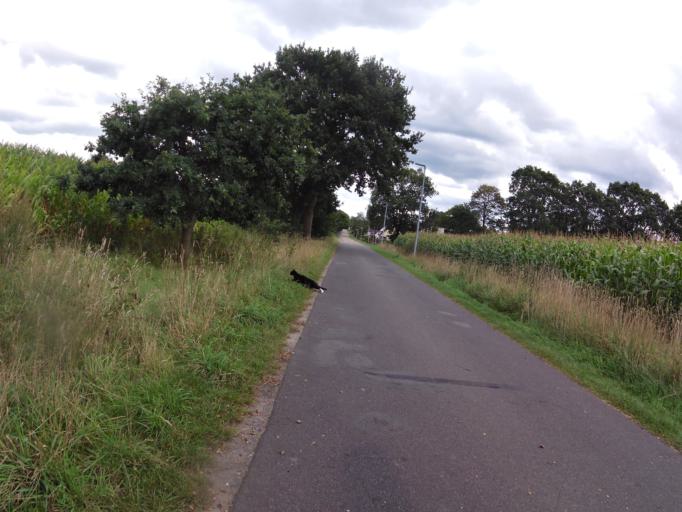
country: DE
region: Lower Saxony
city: Kohlen
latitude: 53.5109
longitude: 8.8594
